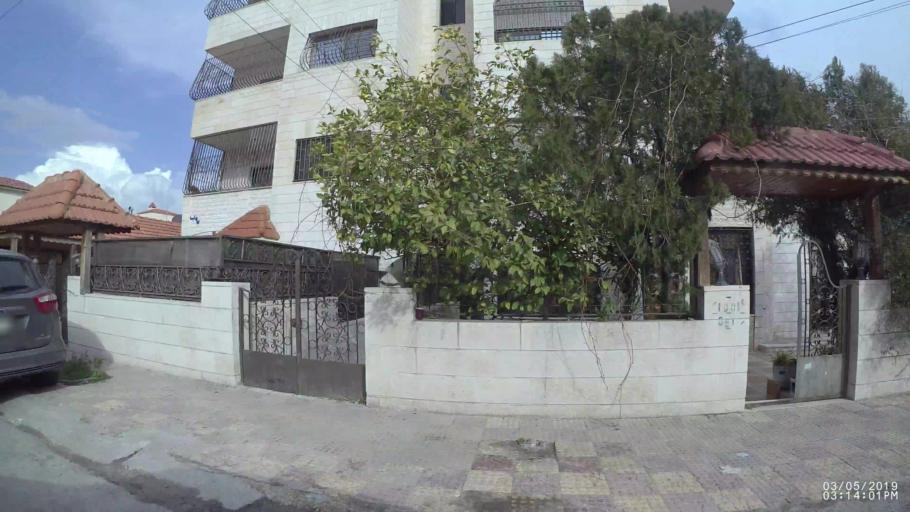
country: JO
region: Amman
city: Amman
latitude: 32.0013
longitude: 35.9451
